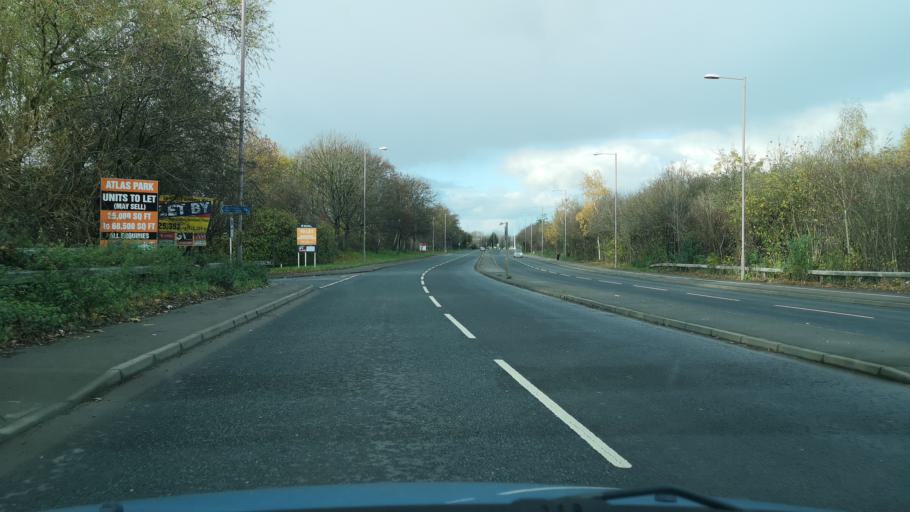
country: GB
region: England
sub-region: City and Borough of Wakefield
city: Normanton
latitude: 53.7016
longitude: -1.3944
